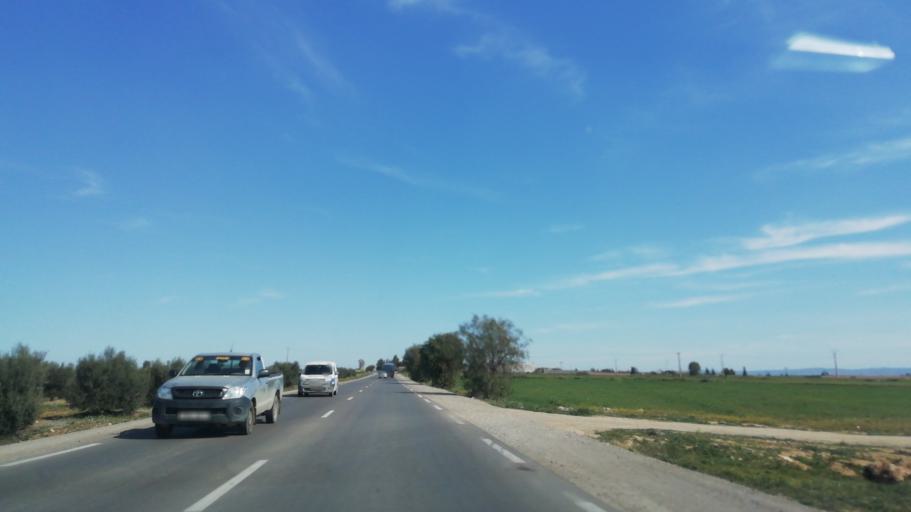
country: DZ
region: Mascara
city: Mascara
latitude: 35.4146
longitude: 0.3777
